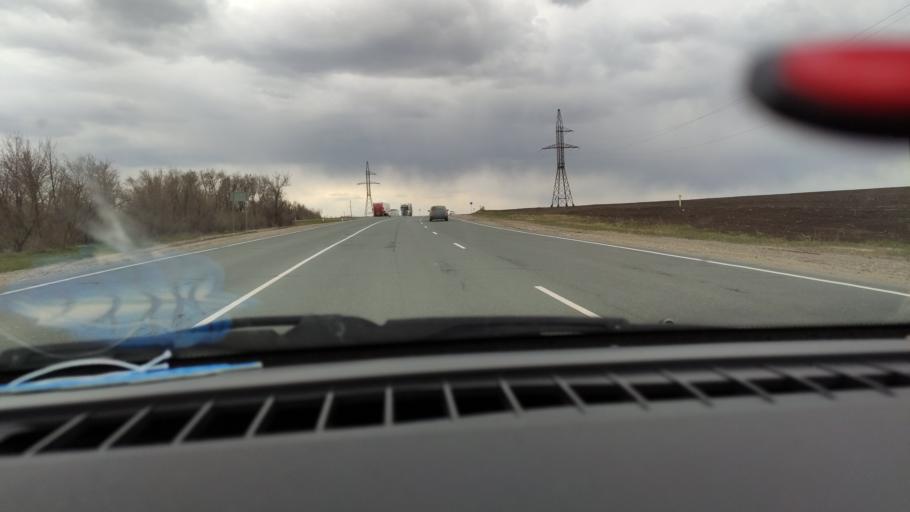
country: RU
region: Saratov
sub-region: Saratovskiy Rayon
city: Saratov
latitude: 51.7451
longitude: 46.0516
